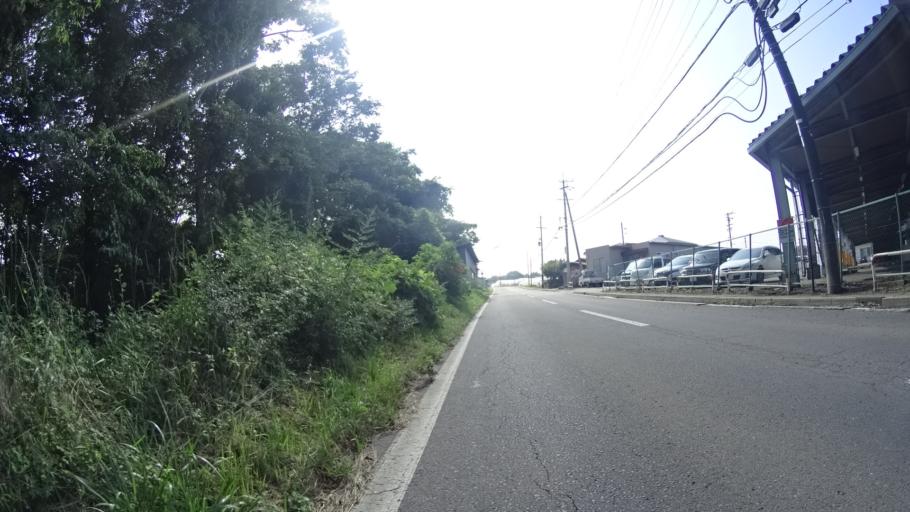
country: JP
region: Nagano
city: Chino
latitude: 35.9612
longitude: 138.2221
